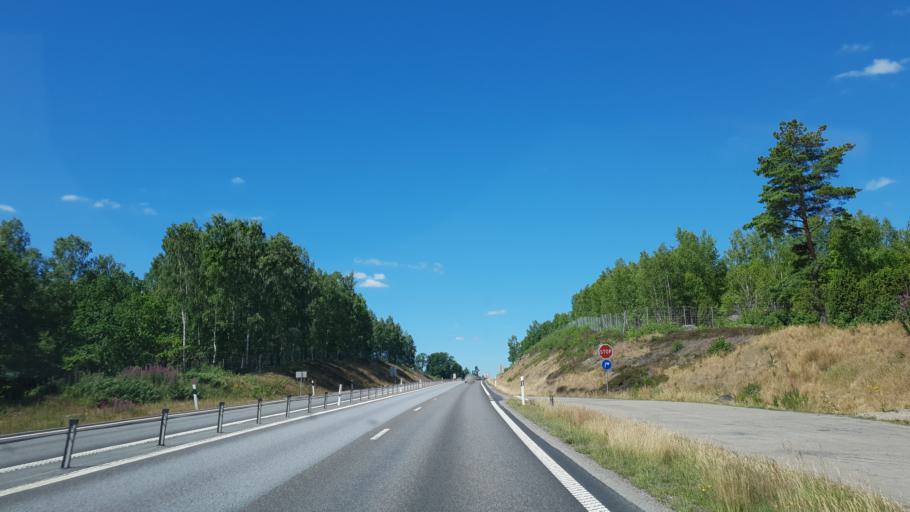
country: SE
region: Kronoberg
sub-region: Alvesta Kommun
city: Alvesta
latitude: 56.9207
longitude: 14.5879
